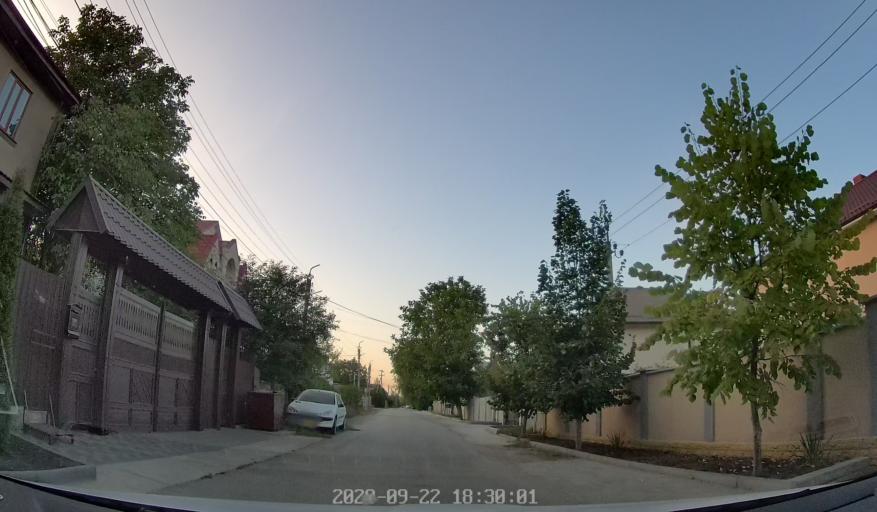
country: MD
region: Laloveni
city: Ialoveni
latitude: 46.9557
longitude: 28.7622
